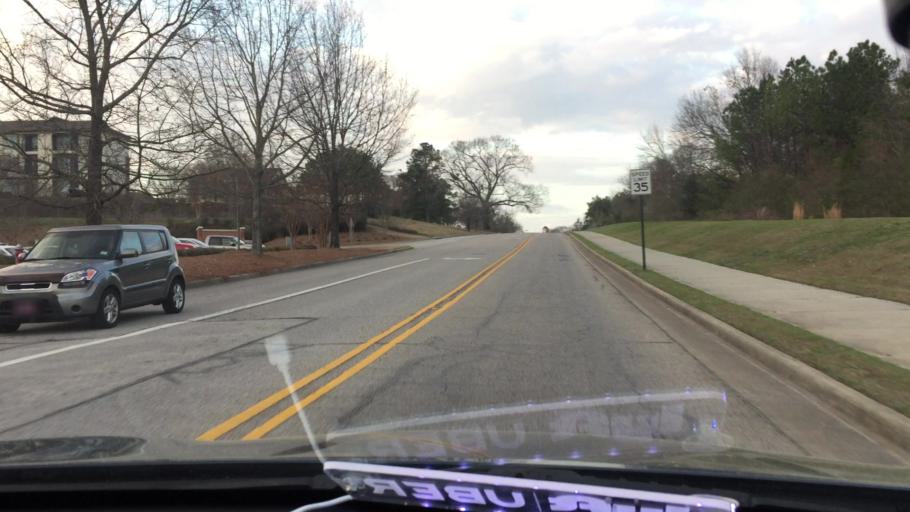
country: US
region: Alabama
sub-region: Lee County
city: Auburn
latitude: 32.5804
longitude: -85.4882
